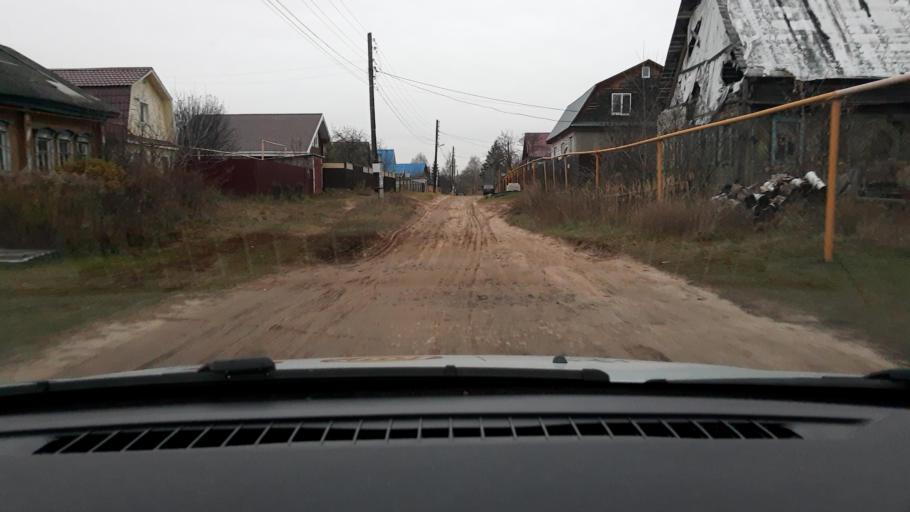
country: RU
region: Nizjnij Novgorod
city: Neklyudovo
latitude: 56.4204
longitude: 44.0208
